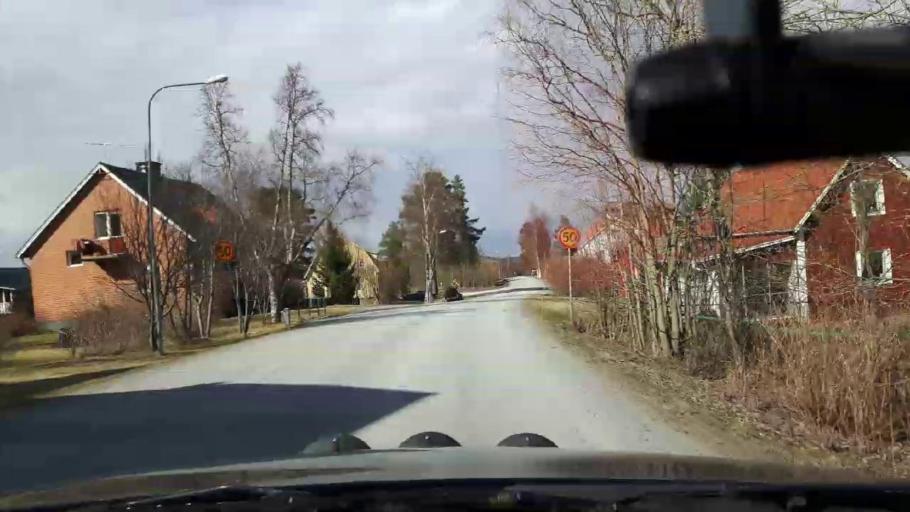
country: SE
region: Jaemtland
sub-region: Bergs Kommun
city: Hoverberg
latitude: 62.9145
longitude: 14.3366
